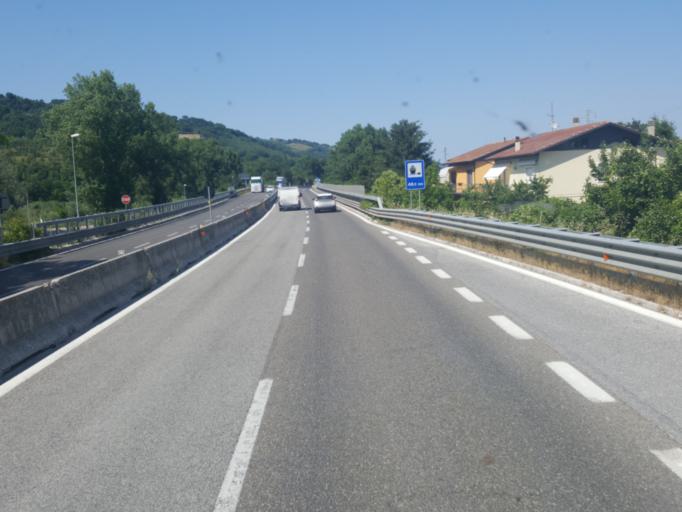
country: IT
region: The Marches
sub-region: Provincia di Ancona
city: Serra San Quirico
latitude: 43.4435
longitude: 13.0316
